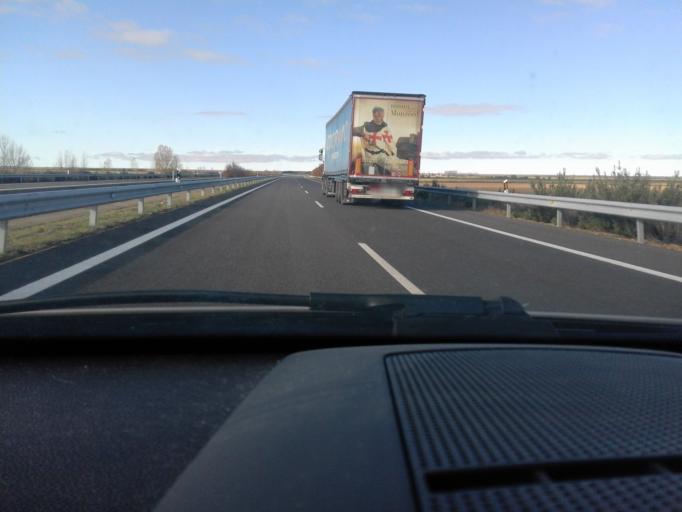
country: ES
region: Castille and Leon
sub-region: Provincia de Palencia
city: Bustillo del Paramo de Carrion
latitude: 42.3461
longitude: -4.7033
